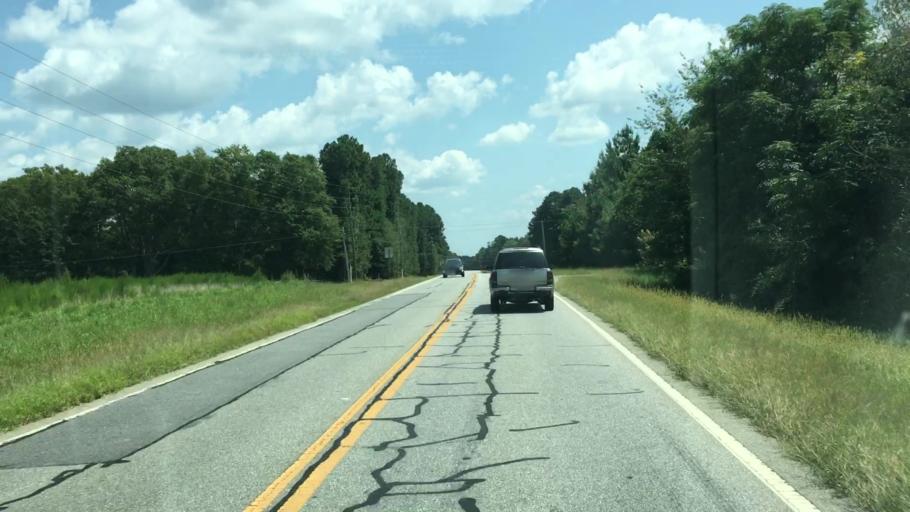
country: US
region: Georgia
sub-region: Barrow County
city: Statham
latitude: 33.9275
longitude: -83.6159
